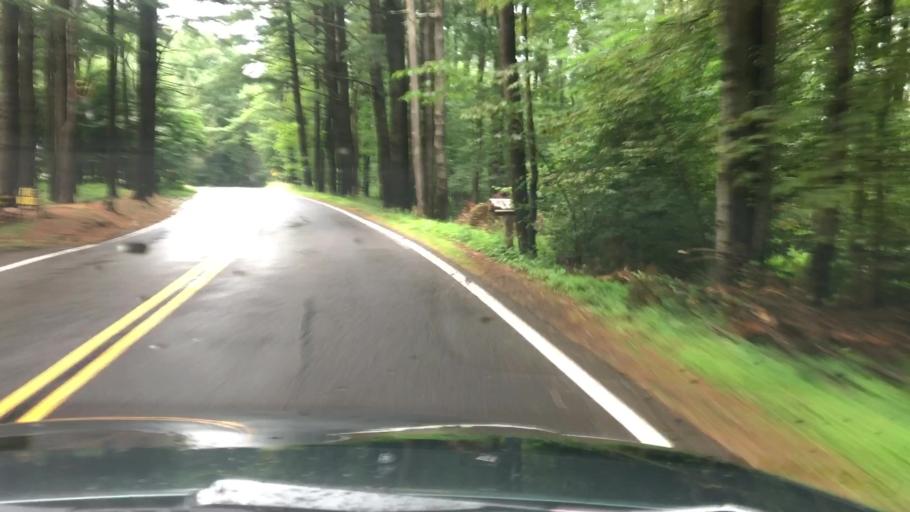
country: US
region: Pennsylvania
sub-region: Monroe County
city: Mountainhome
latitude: 41.3155
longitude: -75.2103
